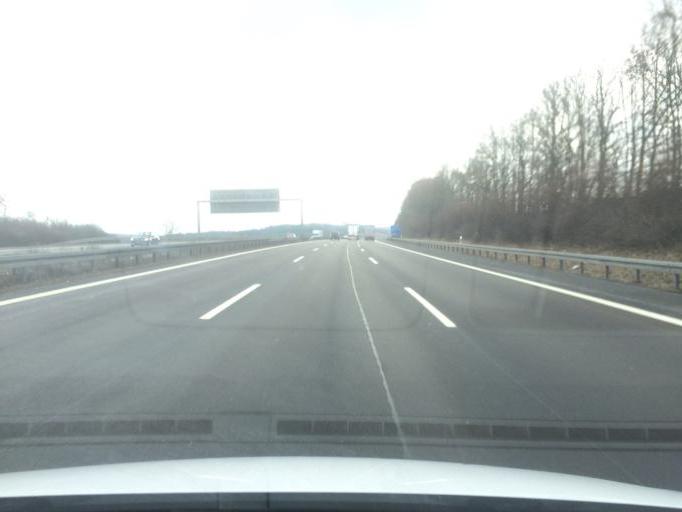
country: DE
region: Bavaria
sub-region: Upper Bavaria
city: Denkendorf
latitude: 48.9249
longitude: 11.4667
